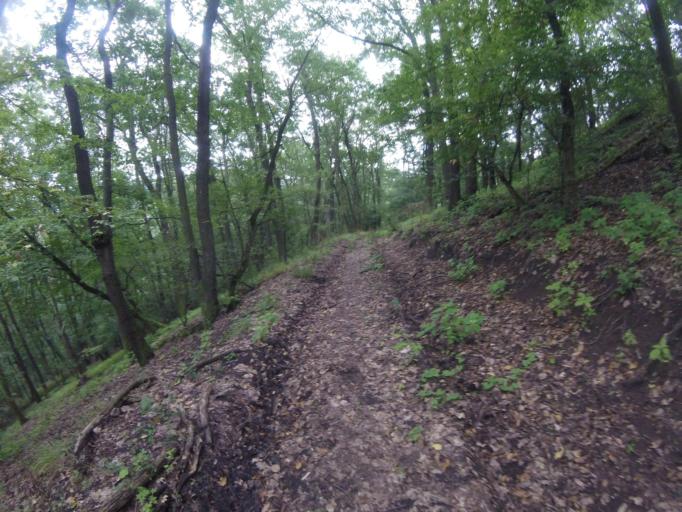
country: SK
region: Nitriansky
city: Sahy
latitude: 48.0471
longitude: 18.9780
